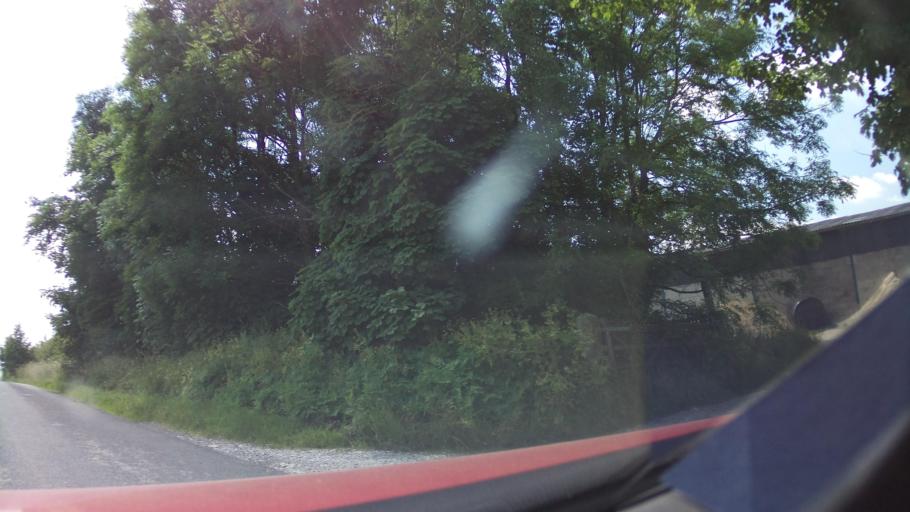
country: GB
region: England
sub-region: Derbyshire
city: Tideswell
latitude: 53.2320
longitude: -1.7862
